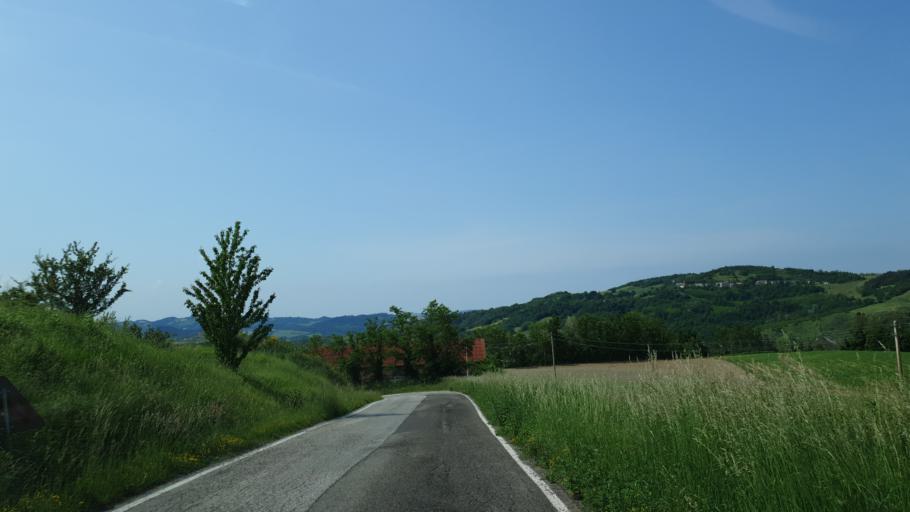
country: IT
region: Emilia-Romagna
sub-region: Provincia di Rimini
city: Sant'Agata Feltria
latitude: 43.9059
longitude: 12.2248
